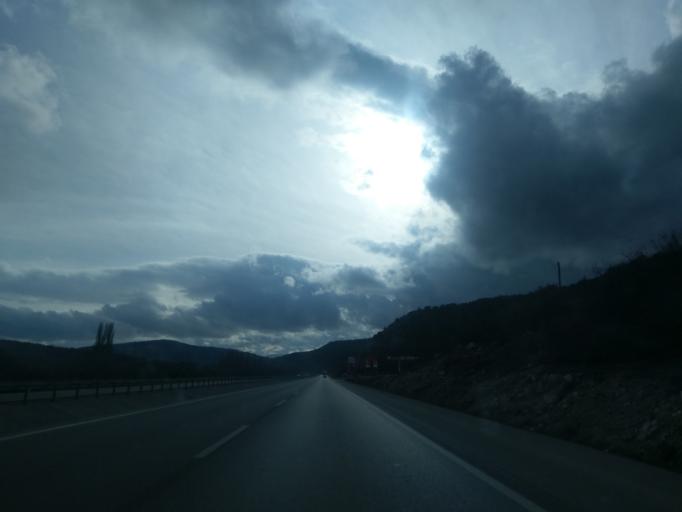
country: TR
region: Kuetahya
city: Sabuncu
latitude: 39.5458
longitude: 30.0578
